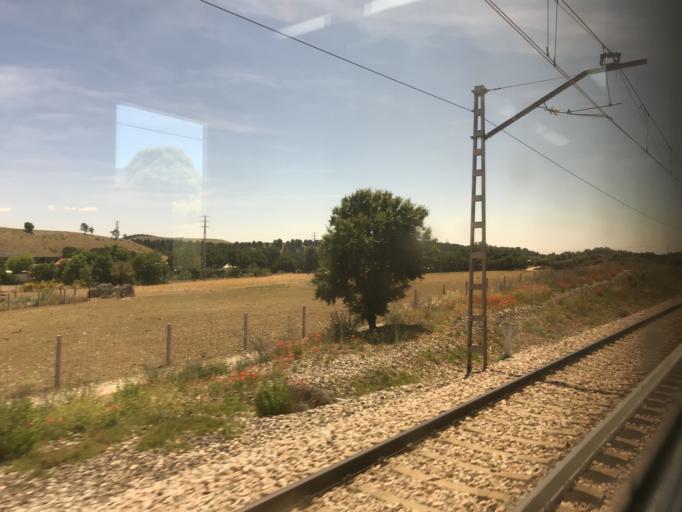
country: ES
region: Madrid
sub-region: Provincia de Madrid
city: Valdemoro
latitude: 40.2061
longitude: -3.6714
